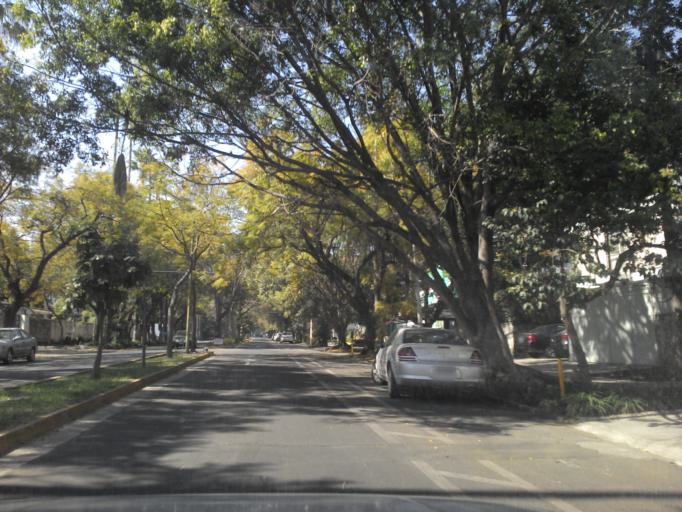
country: MX
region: Jalisco
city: Guadalajara
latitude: 20.6722
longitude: -103.3630
